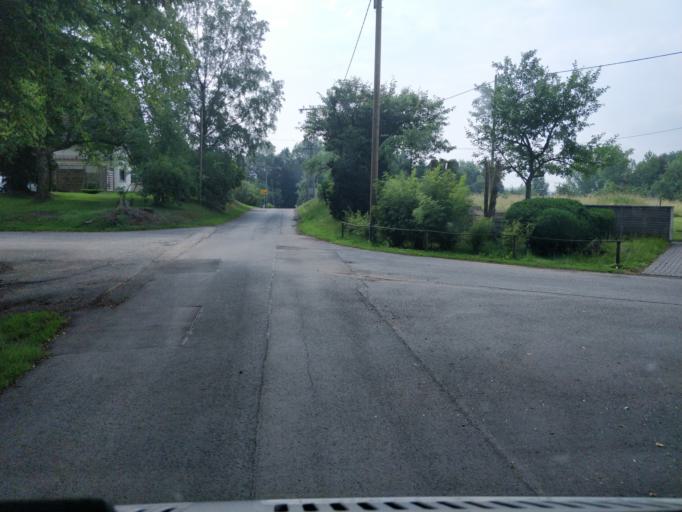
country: DE
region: North Rhine-Westphalia
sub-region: Regierungsbezirk Koln
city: Numbrecht
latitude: 50.9111
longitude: 7.5697
